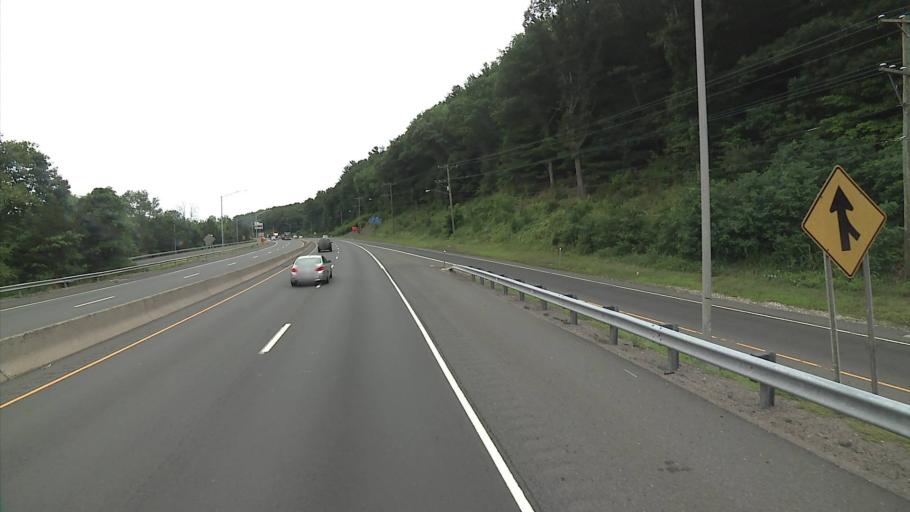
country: US
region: Connecticut
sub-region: New Haven County
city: Naugatuck
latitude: 41.5063
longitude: -73.0455
